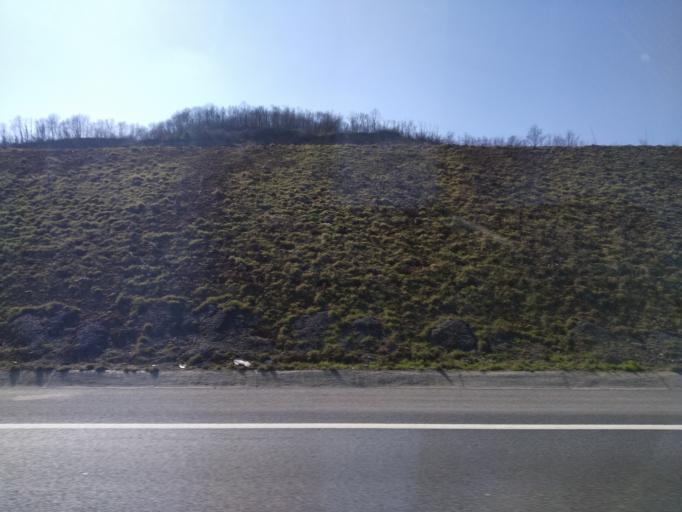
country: TR
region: Istanbul
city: Mahmut Sevket Pasa
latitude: 41.1608
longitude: 29.2594
